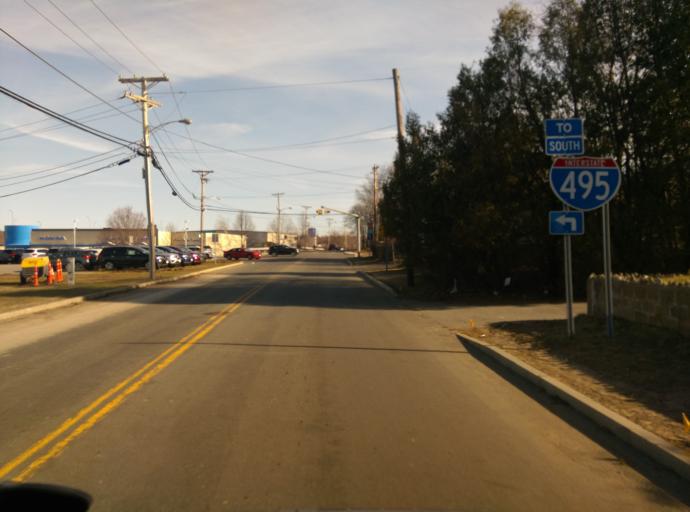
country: US
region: Massachusetts
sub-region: Essex County
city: North Andover
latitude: 42.7146
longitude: -71.1403
